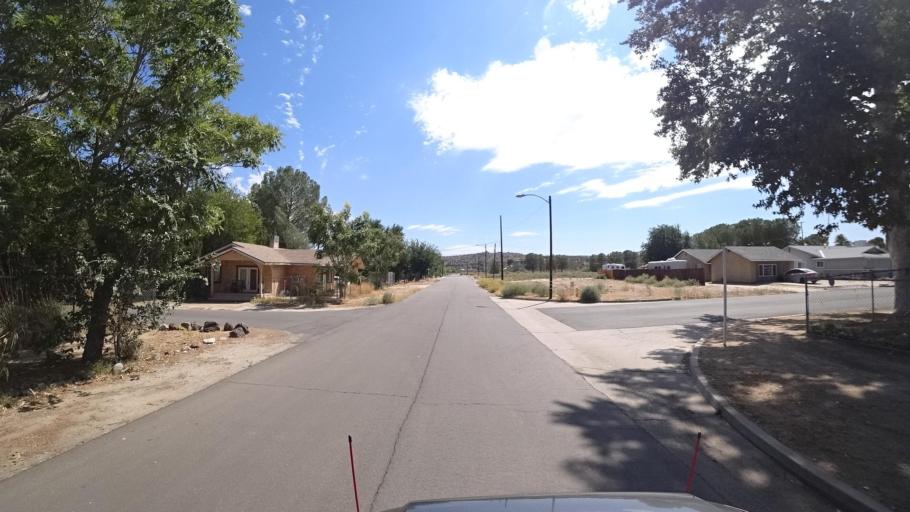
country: MX
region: Baja California
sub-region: Tecate
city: Cereso del Hongo
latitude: 32.6193
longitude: -116.1874
